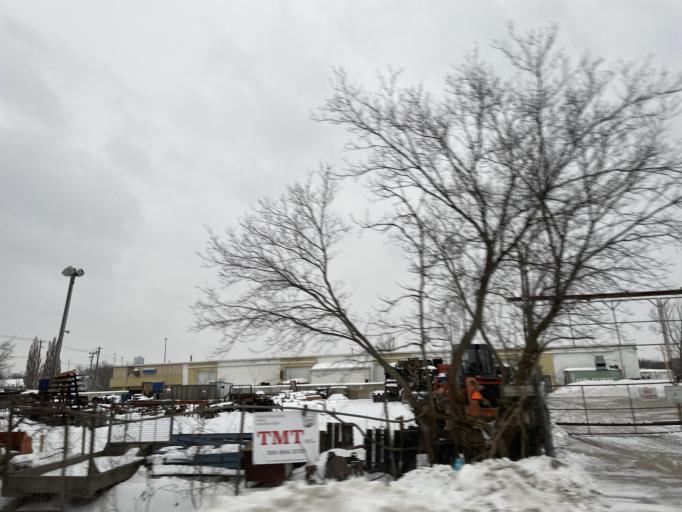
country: CA
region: Ontario
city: Waterloo
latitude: 43.4701
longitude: -80.4711
